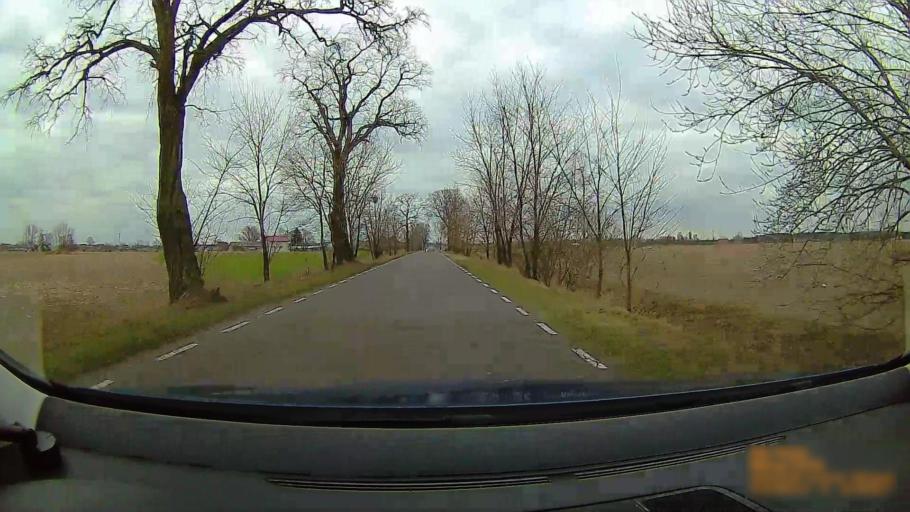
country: PL
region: Greater Poland Voivodeship
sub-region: Powiat koninski
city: Rzgow Pierwszy
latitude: 52.1117
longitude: 18.0753
